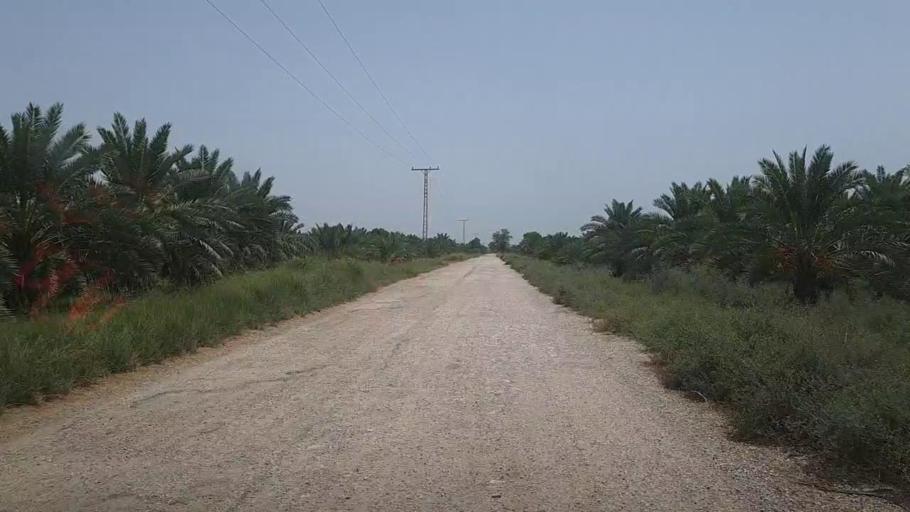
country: PK
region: Sindh
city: Pad Idan
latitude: 26.8487
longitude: 68.3247
